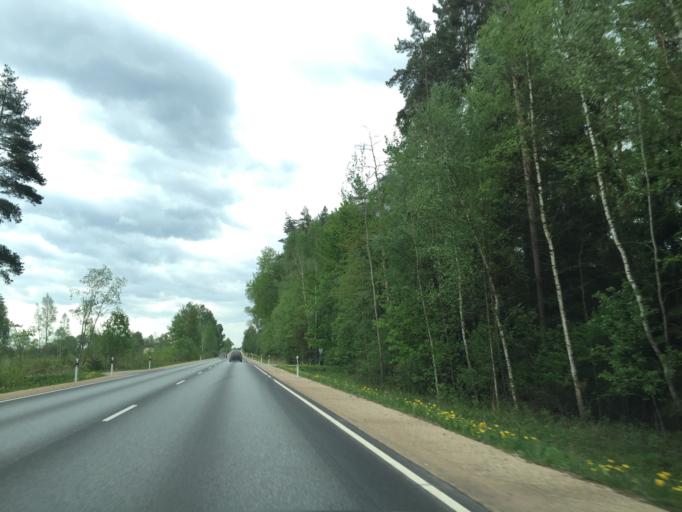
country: LV
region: Ikskile
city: Ikskile
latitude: 56.8745
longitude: 24.5317
